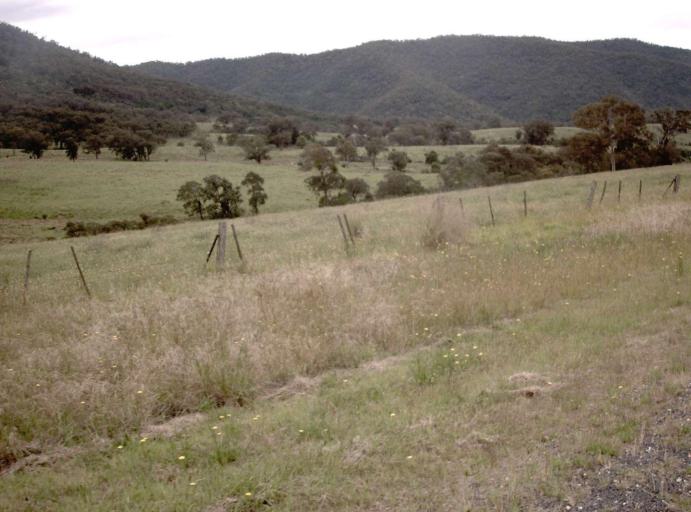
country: AU
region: Victoria
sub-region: East Gippsland
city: Bairnsdale
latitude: -37.5665
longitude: 147.1876
